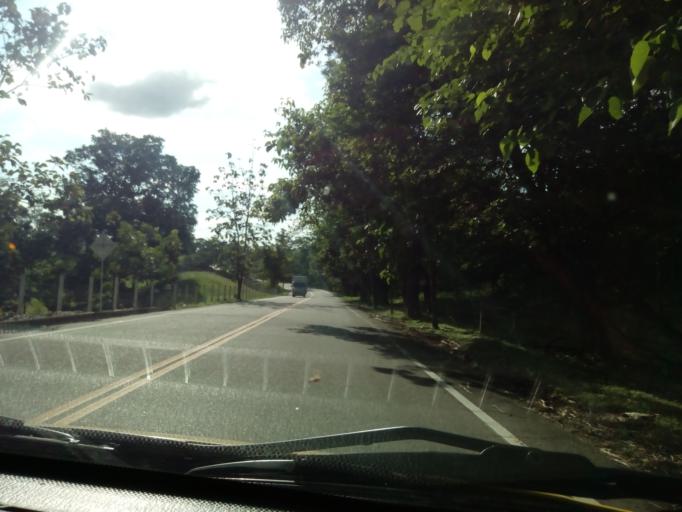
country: CO
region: Boyaca
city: Puerto Boyaca
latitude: 5.9527
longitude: -74.4897
